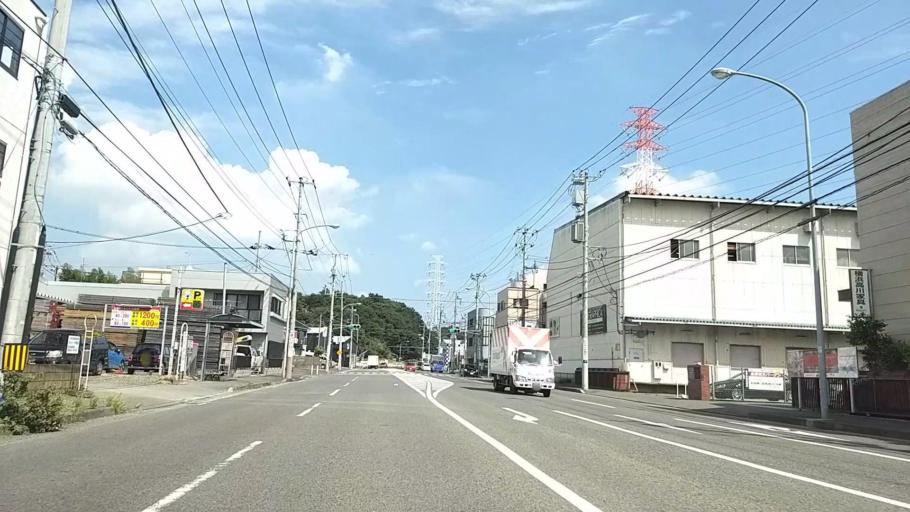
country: JP
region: Kanagawa
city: Yokohama
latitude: 35.5223
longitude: 139.5980
